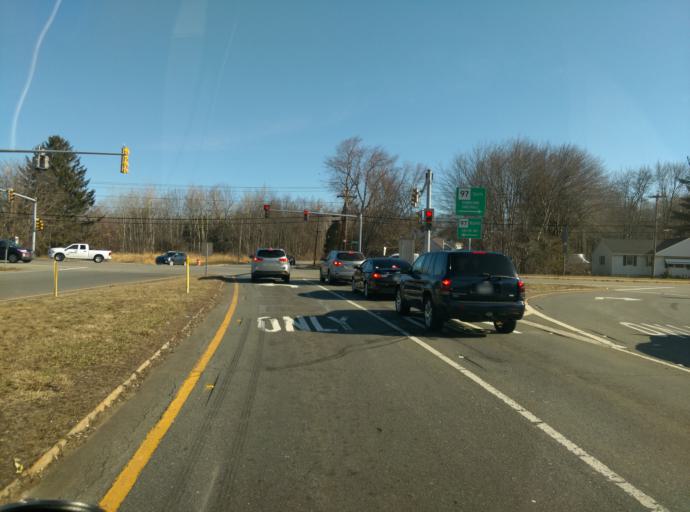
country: US
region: Massachusetts
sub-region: Essex County
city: Haverhill
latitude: 42.7822
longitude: -71.1131
